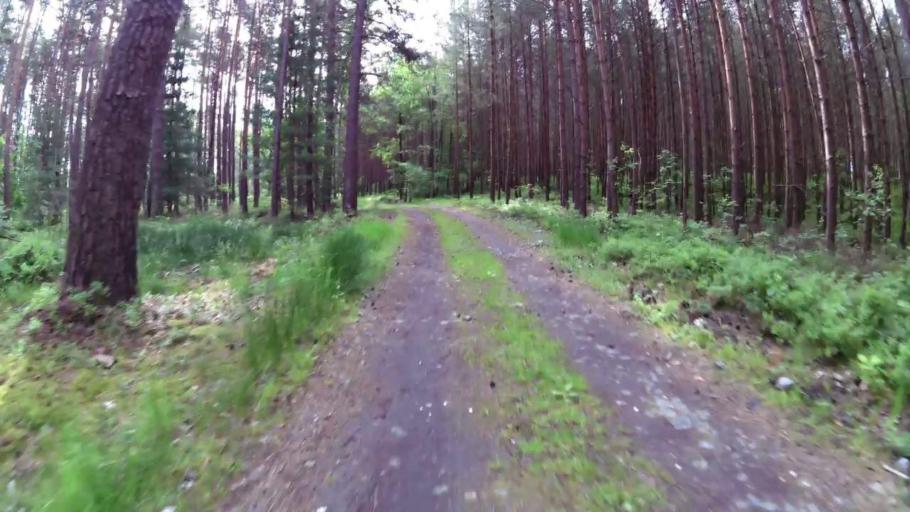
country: PL
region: West Pomeranian Voivodeship
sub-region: Swinoujscie
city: Swinoujscie
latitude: 53.9097
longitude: 14.3131
